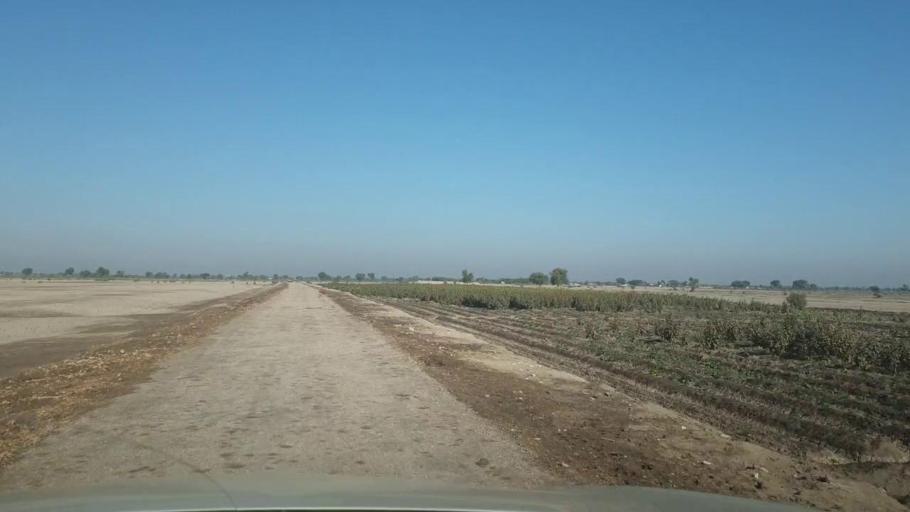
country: PK
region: Sindh
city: Bhan
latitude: 26.5213
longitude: 67.6744
